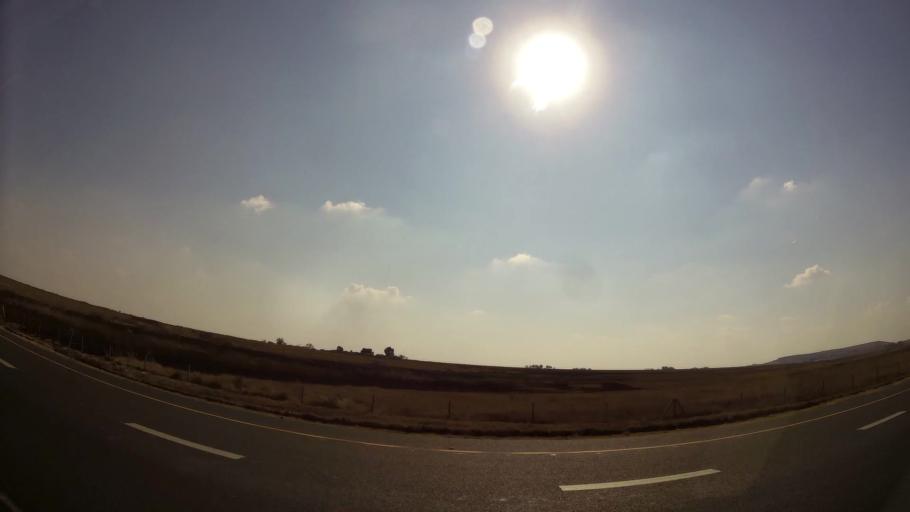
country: ZA
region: Gauteng
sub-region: Ekurhuleni Metropolitan Municipality
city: Springs
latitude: -26.1638
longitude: 28.4989
